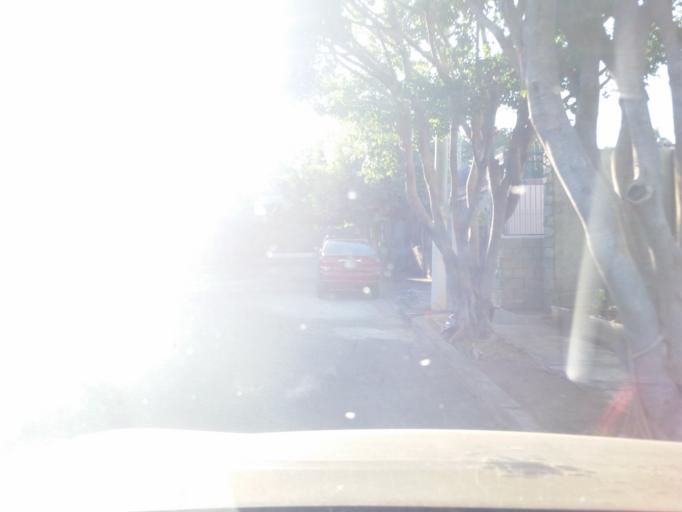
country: NI
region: Managua
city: Managua
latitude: 12.0998
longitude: -86.2554
